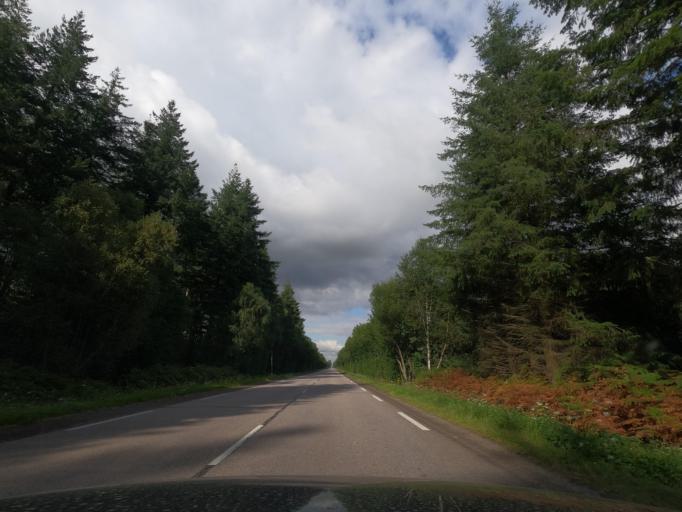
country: FR
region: Lower Normandy
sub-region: Departement de l'Orne
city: Gace
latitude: 48.8415
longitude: 0.3470
